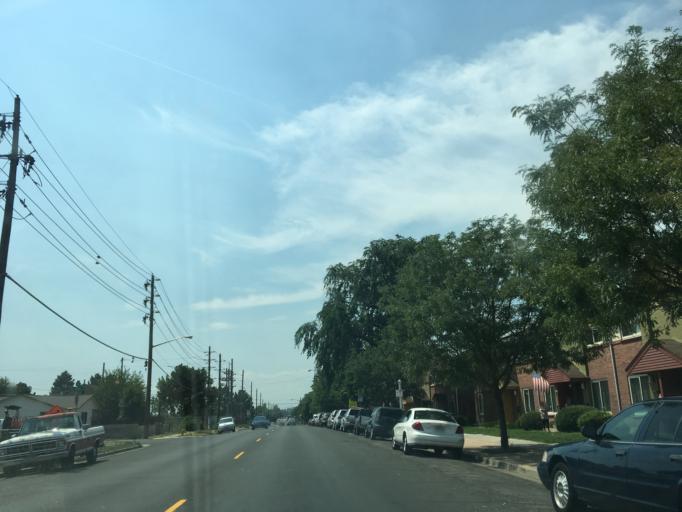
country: US
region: Colorado
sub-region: Jefferson County
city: Lakewood
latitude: 39.7018
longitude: -105.0299
